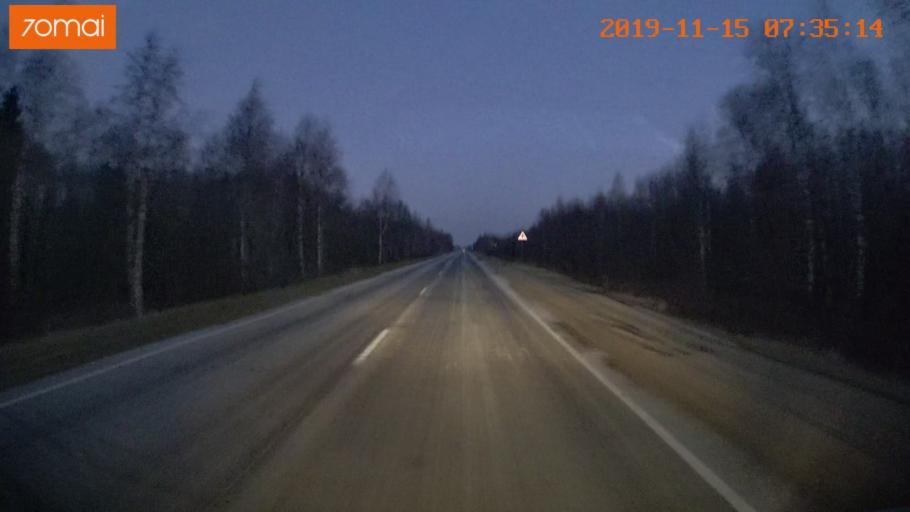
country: RU
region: Vologda
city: Sheksna
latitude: 58.7283
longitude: 38.4550
